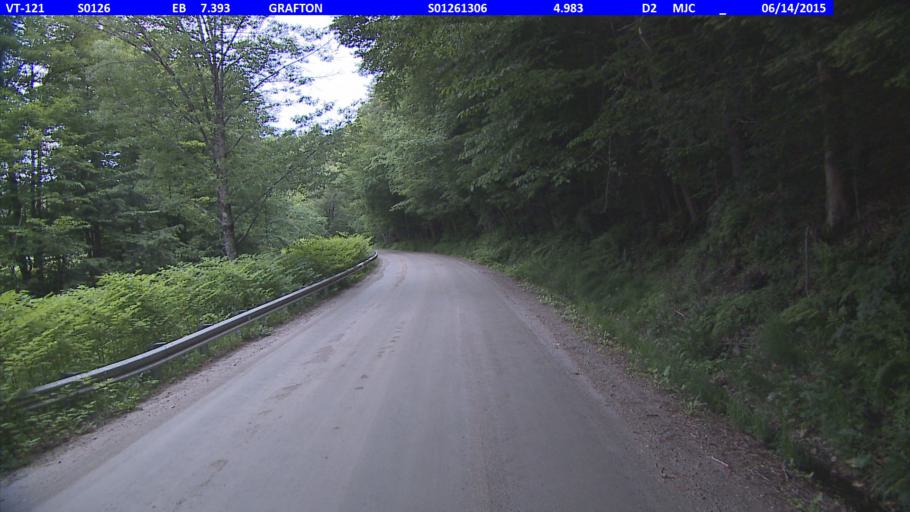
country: US
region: Vermont
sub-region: Windsor County
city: Chester
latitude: 43.1793
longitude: -72.6121
